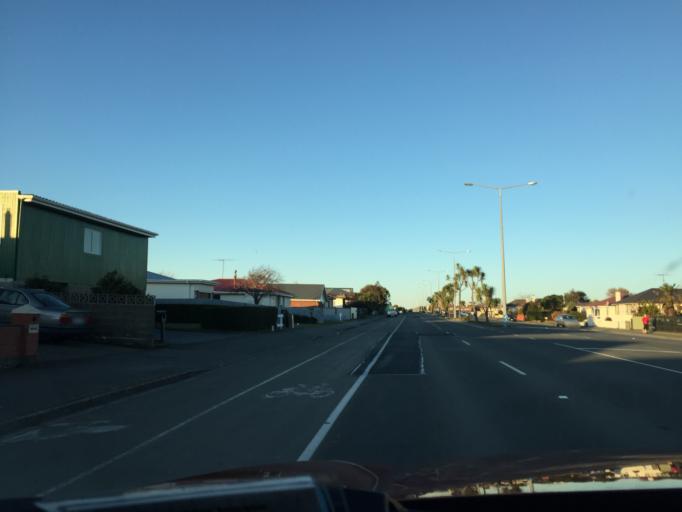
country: NZ
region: Southland
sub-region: Invercargill City
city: Invercargill
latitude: -46.4178
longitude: 168.3824
